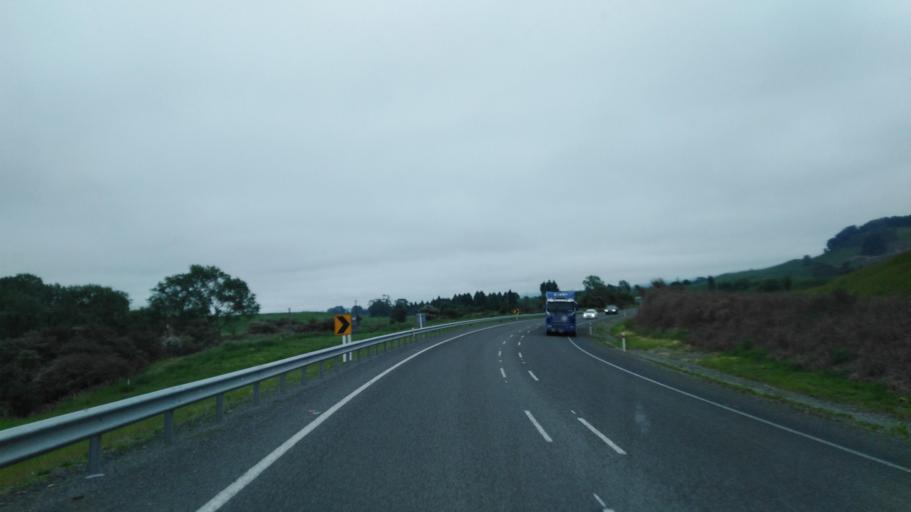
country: NZ
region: Bay of Plenty
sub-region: Rotorua District
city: Rotorua
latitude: -38.3634
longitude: 176.3569
